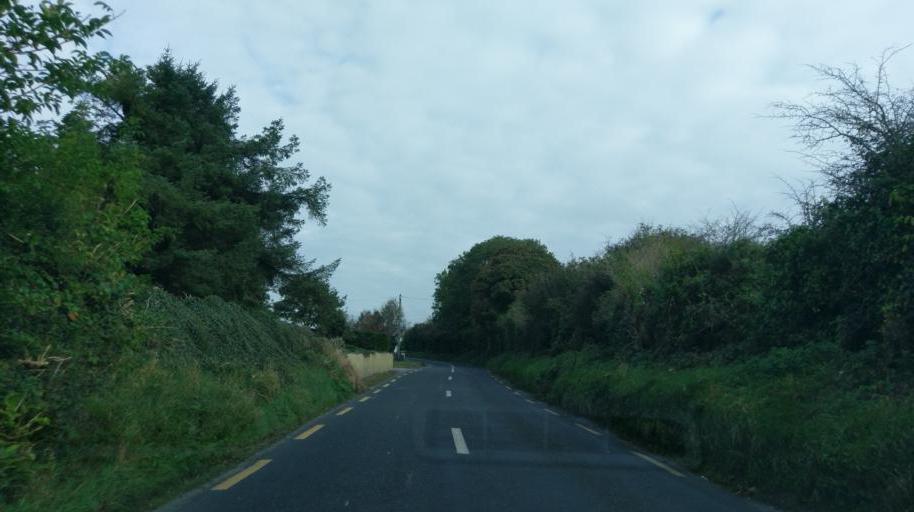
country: IE
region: Connaught
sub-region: County Galway
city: Athenry
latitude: 53.3177
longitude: -8.7303
